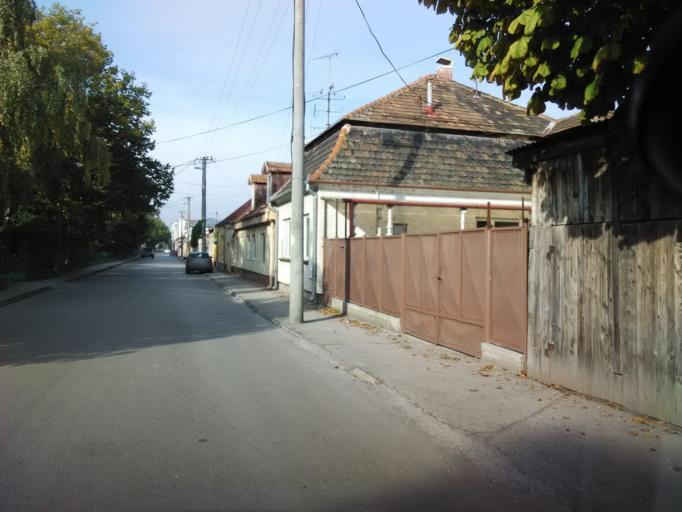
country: SK
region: Nitriansky
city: Komarno
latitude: 47.7659
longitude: 18.1310
